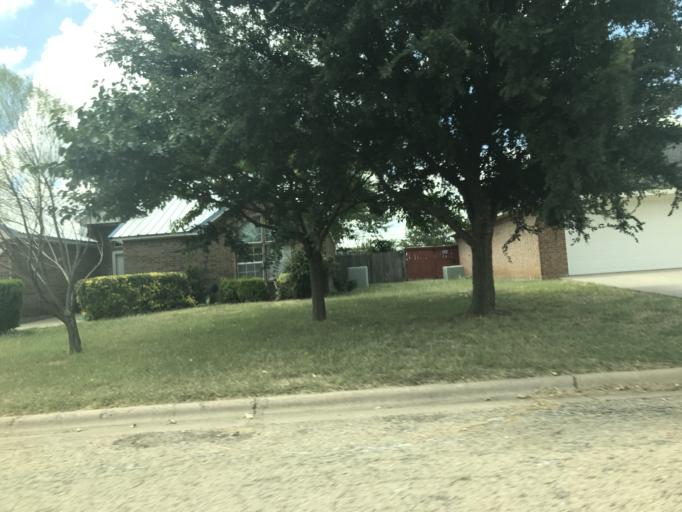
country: US
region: Texas
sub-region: Taylor County
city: Abilene
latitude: 32.4378
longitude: -99.6985
